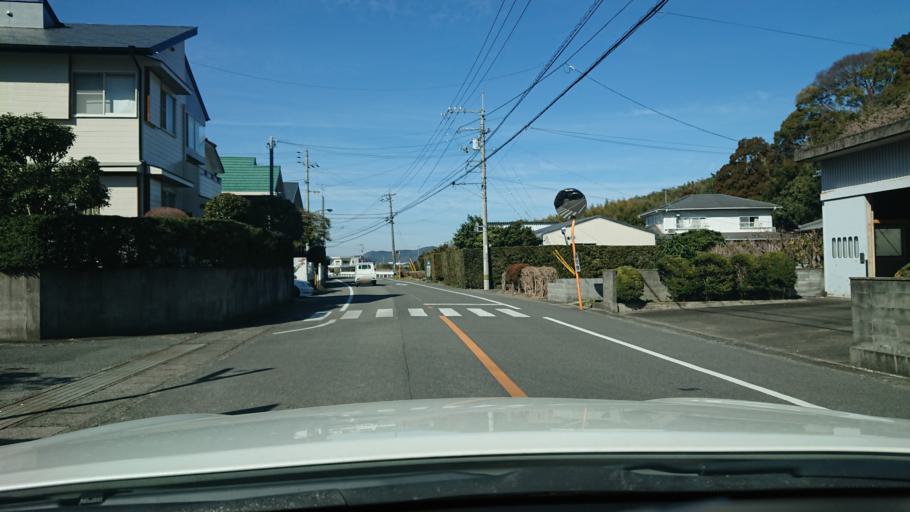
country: JP
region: Tokushima
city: Komatsushimacho
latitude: 33.9746
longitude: 134.5907
